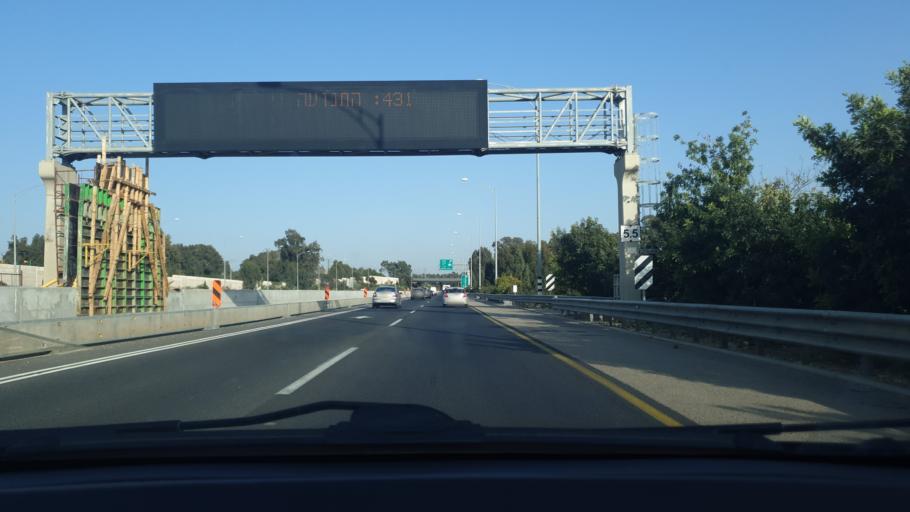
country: IL
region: Central District
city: Ness Ziona
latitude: 31.9292
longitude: 34.8243
